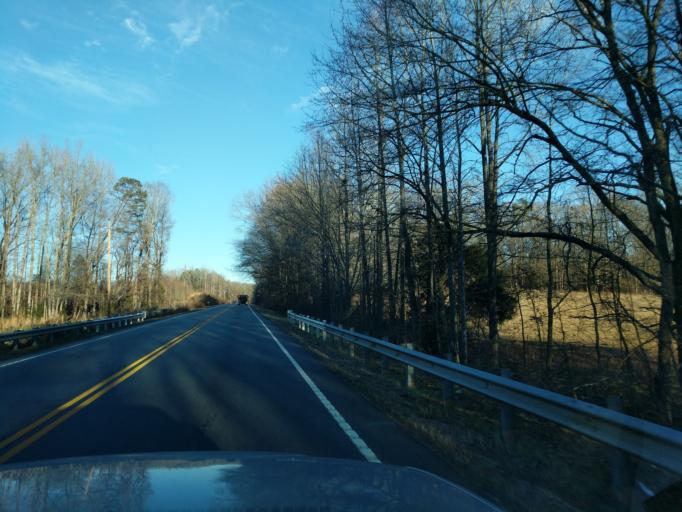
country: US
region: South Carolina
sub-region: Greenville County
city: Simpsonville
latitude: 34.6531
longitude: -82.2967
